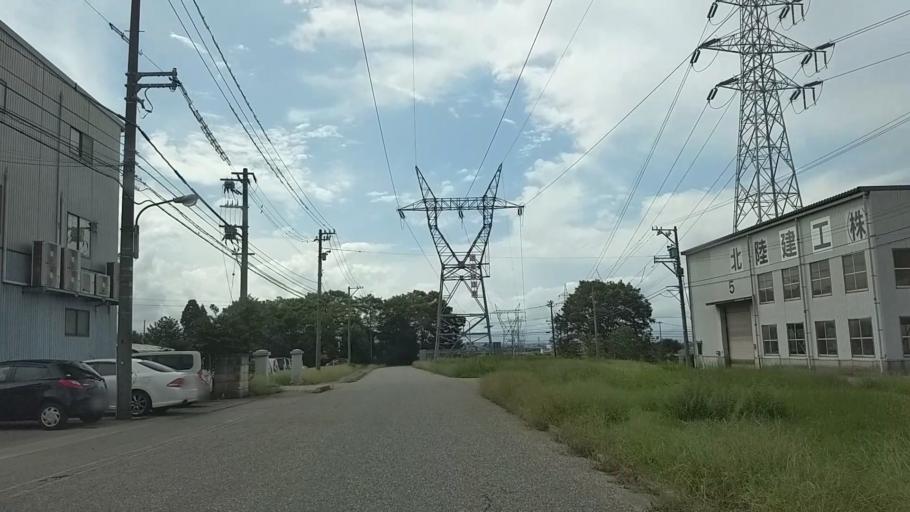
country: JP
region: Toyama
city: Kamiichi
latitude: 36.7386
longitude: 137.3750
